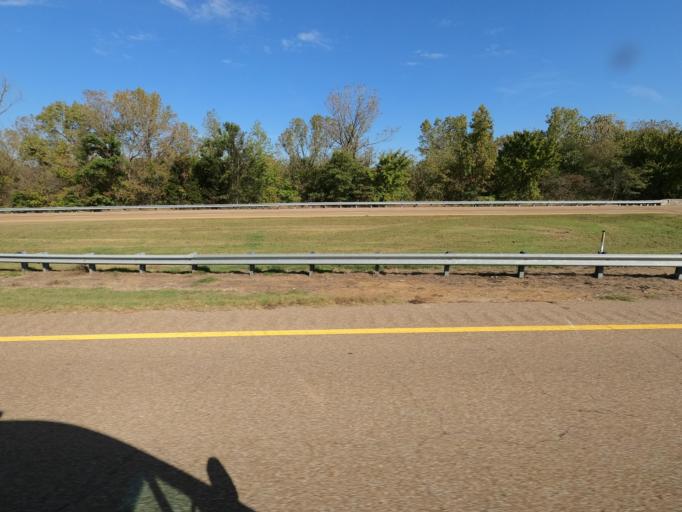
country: US
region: Tennessee
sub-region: Shelby County
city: Millington
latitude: 35.3302
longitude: -89.9039
